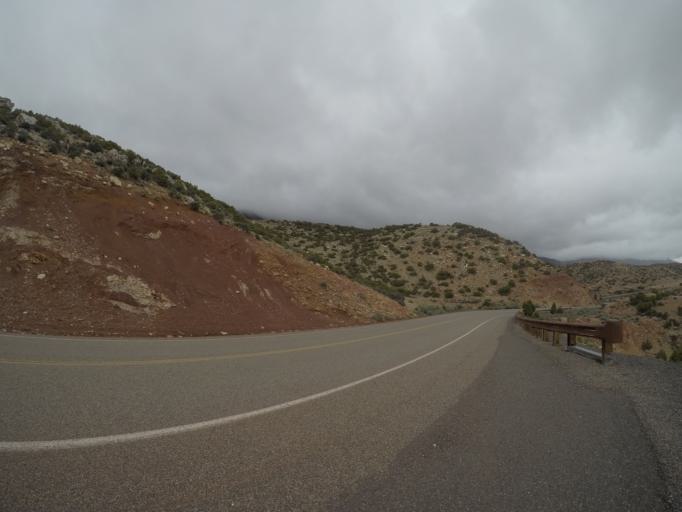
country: US
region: Wyoming
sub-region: Big Horn County
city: Lovell
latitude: 45.0433
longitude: -108.2519
